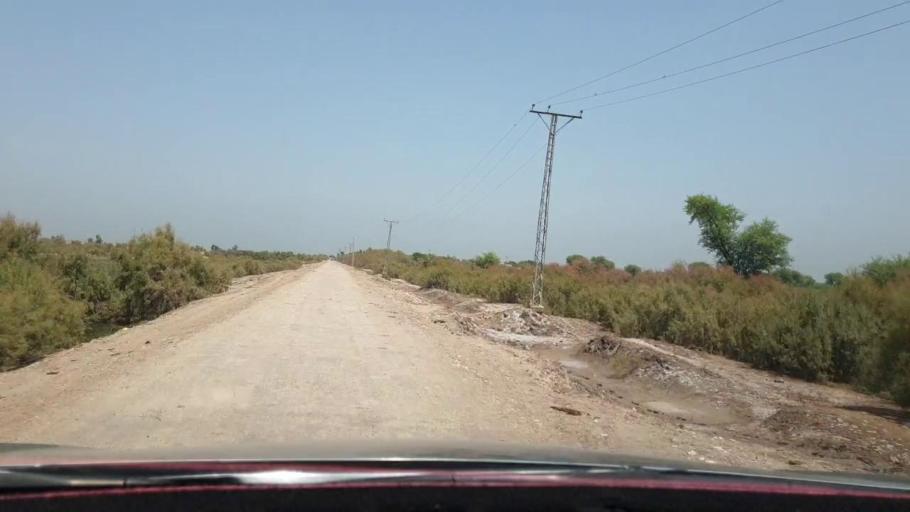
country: PK
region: Sindh
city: Warah
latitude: 27.4054
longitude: 67.6930
